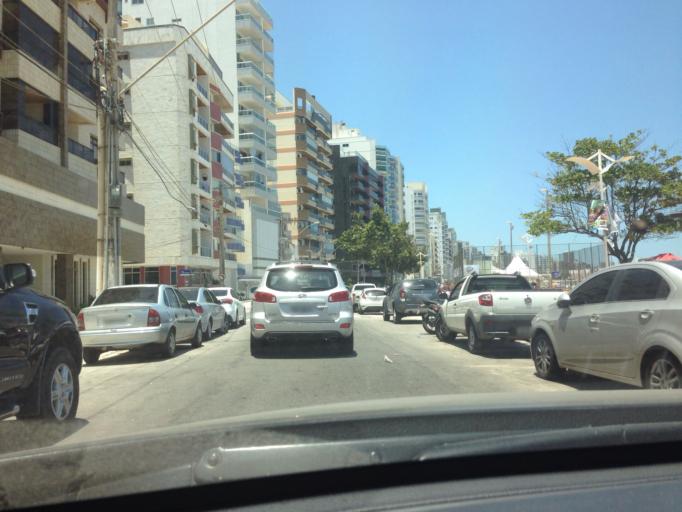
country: BR
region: Espirito Santo
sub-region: Guarapari
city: Guarapari
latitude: -20.6596
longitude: -40.4949
